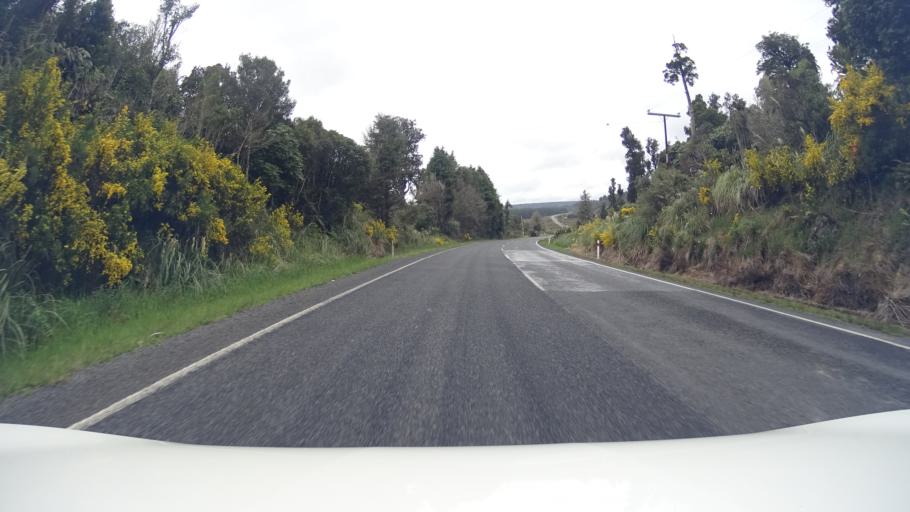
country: NZ
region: Manawatu-Wanganui
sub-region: Ruapehu District
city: Waiouru
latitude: -39.2366
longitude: 175.3916
